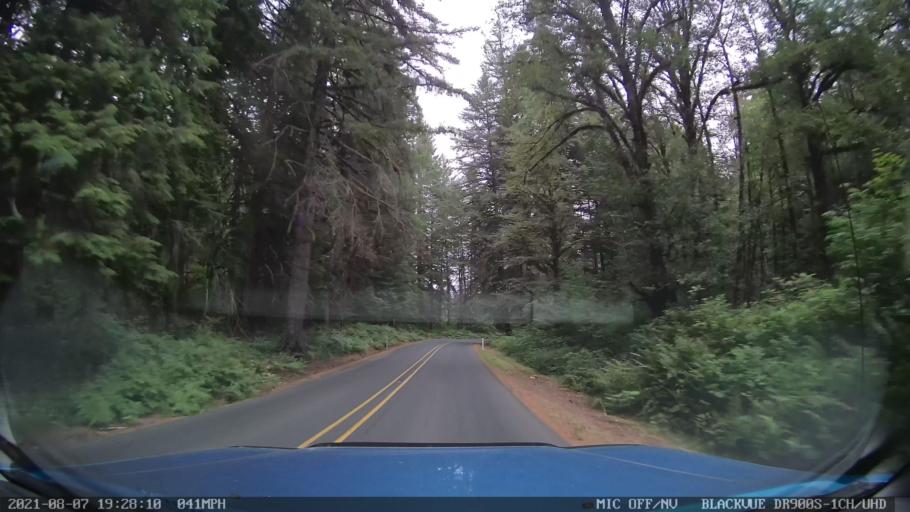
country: US
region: Oregon
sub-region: Linn County
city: Lyons
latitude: 44.8827
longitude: -122.6412
